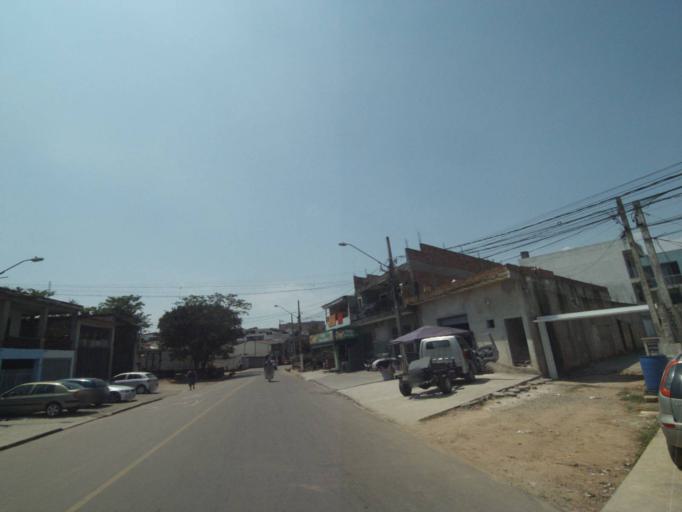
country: BR
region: Parana
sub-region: Curitiba
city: Curitiba
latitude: -25.4835
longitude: -49.3134
